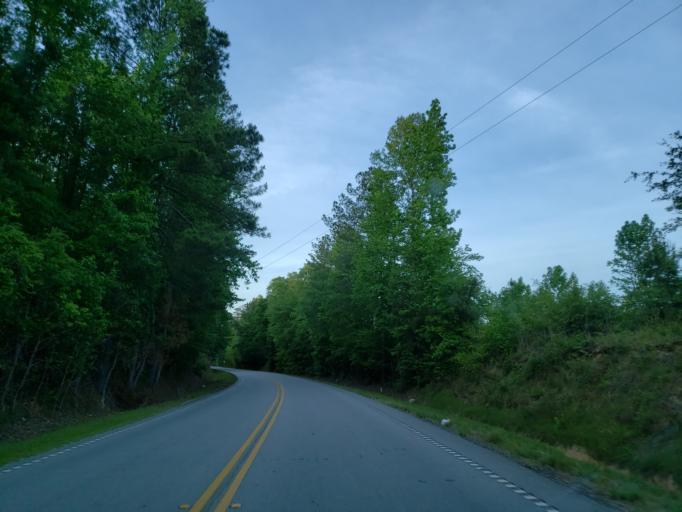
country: US
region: Georgia
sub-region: Fulton County
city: Chattahoochee Hills
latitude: 33.5121
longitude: -84.8837
